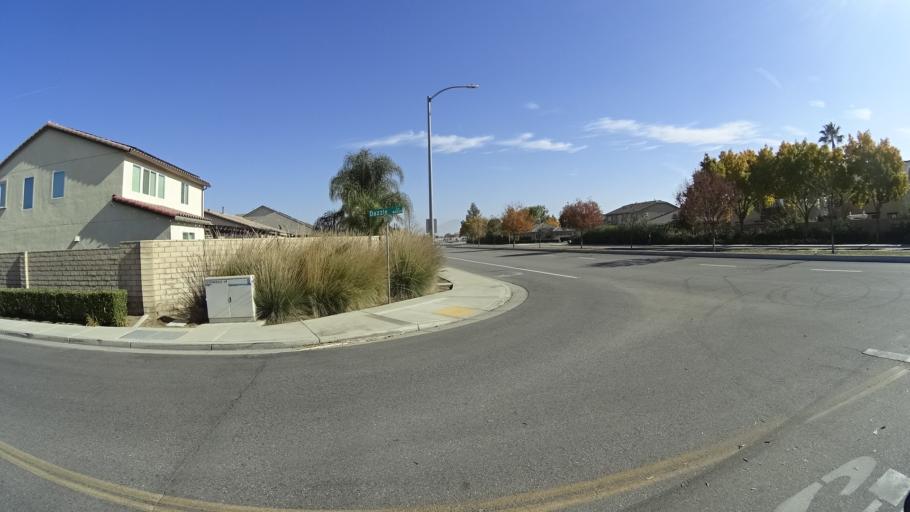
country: US
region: California
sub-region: Kern County
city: Greenfield
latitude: 35.2817
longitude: -119.0603
